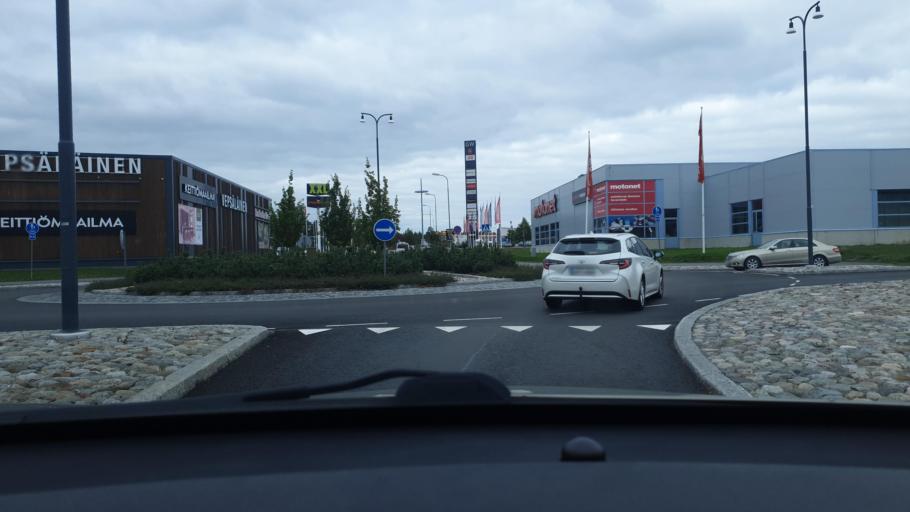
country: FI
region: Ostrobothnia
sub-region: Vaasa
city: Korsholm
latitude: 63.1114
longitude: 21.6536
